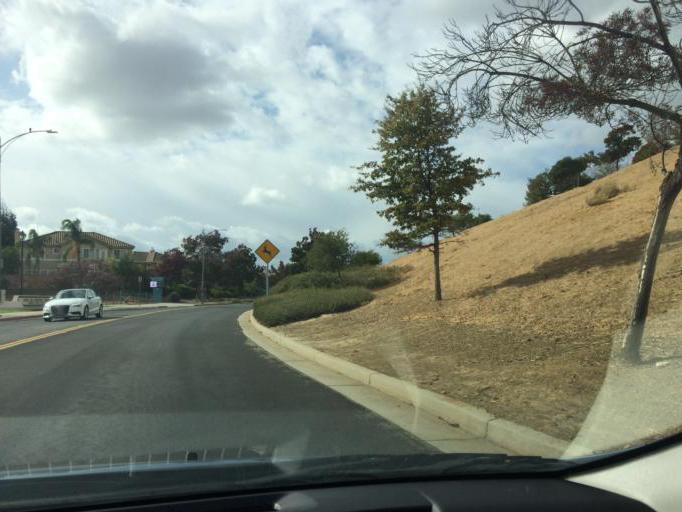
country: US
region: California
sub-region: Santa Clara County
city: Seven Trees
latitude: 37.2806
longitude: -121.7600
